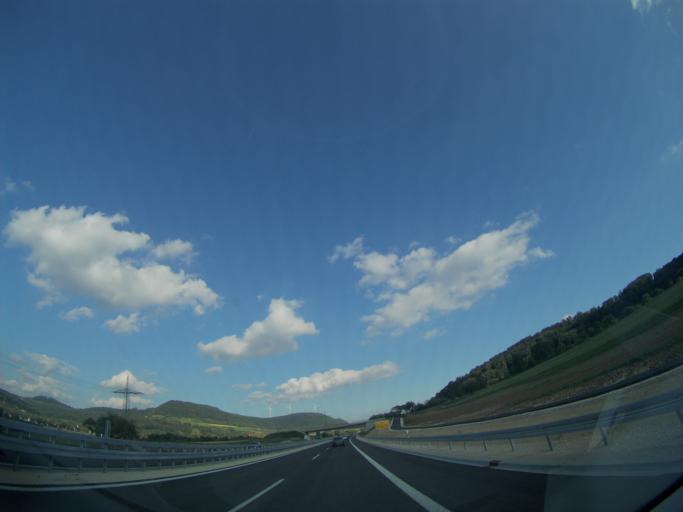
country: DE
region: Baden-Wuerttemberg
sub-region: Regierungsbezirk Stuttgart
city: Gingen an der Fils
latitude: 48.6632
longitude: 9.7651
